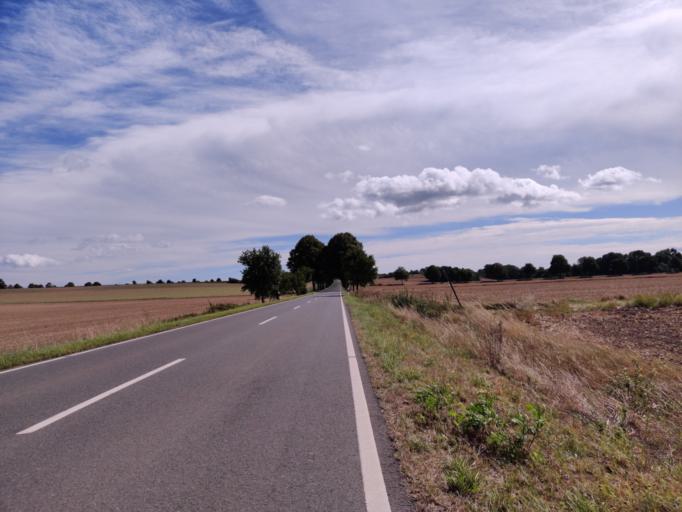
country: DE
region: Lower Saxony
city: Sehlde
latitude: 52.0389
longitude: 10.2838
